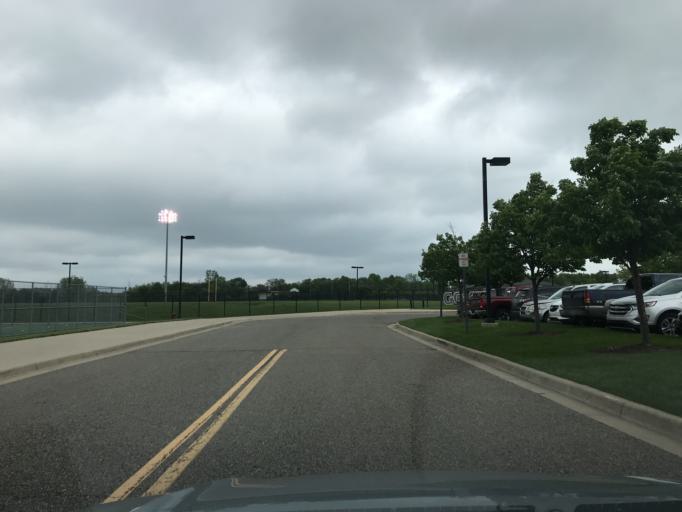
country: US
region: Michigan
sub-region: Oakland County
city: Wixom
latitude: 42.4666
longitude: -83.5680
